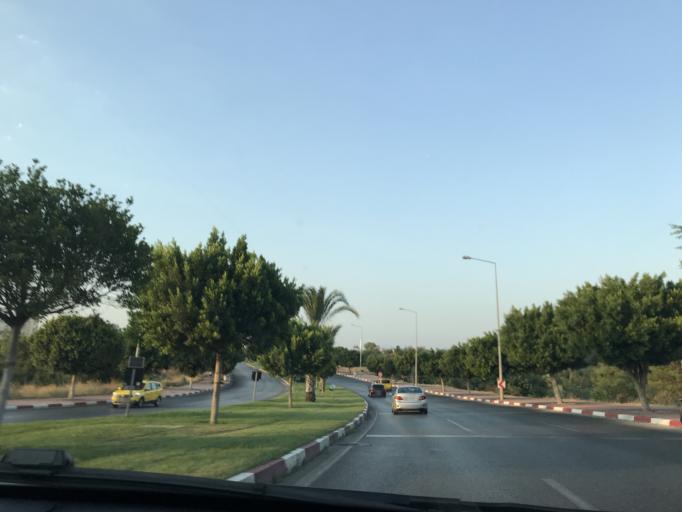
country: TR
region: Antalya
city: Antalya
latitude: 36.8687
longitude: 30.6396
